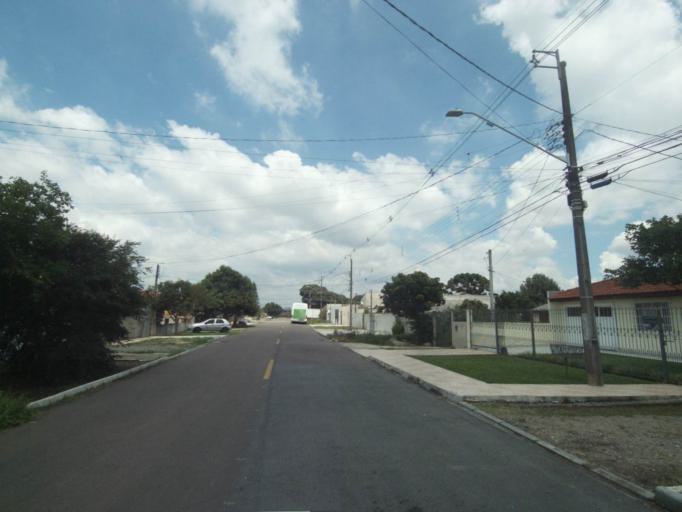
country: BR
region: Parana
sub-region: Pinhais
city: Pinhais
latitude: -25.4786
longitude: -49.1944
